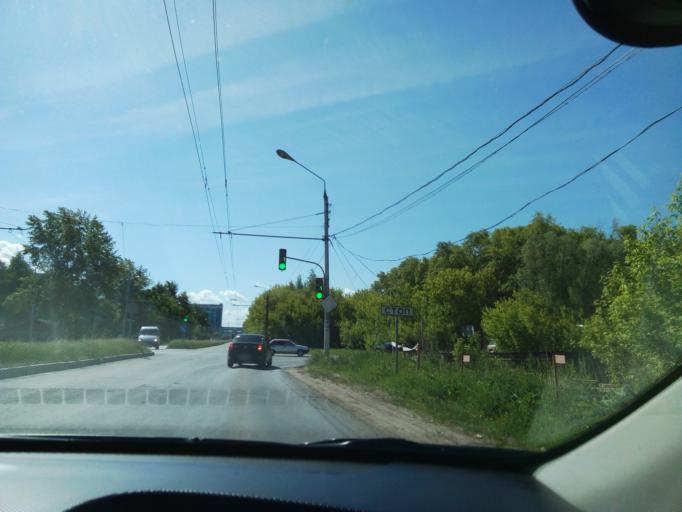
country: RU
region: Chuvashia
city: Novocheboksarsk
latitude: 56.0816
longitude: 47.5058
